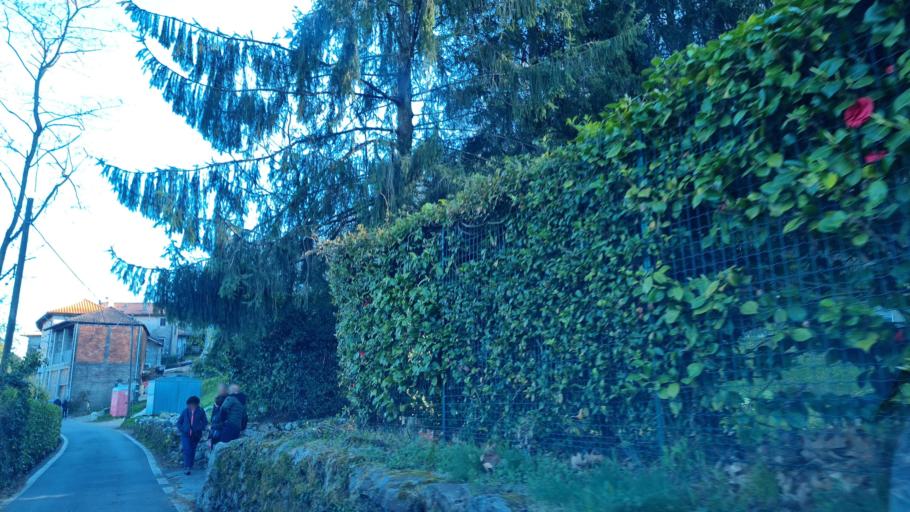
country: IT
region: Piedmont
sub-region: Provincia di Novara
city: San Maurizio D'Opaglio
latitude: 45.7766
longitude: 8.4086
